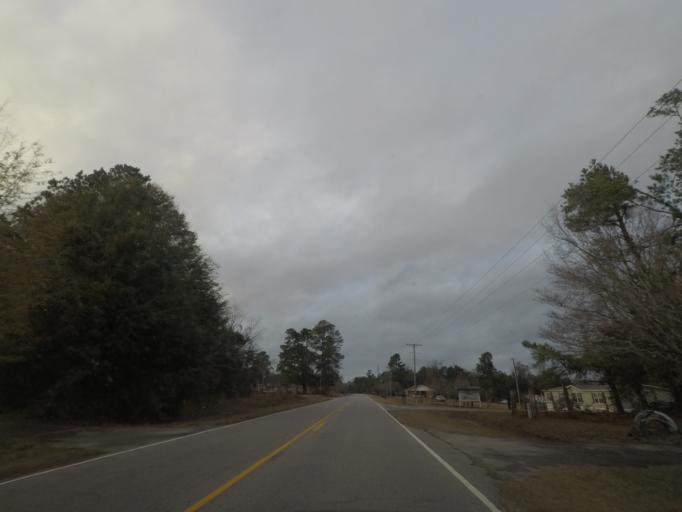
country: US
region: South Carolina
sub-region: Dorchester County
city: Saint George
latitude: 33.0774
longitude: -80.6406
